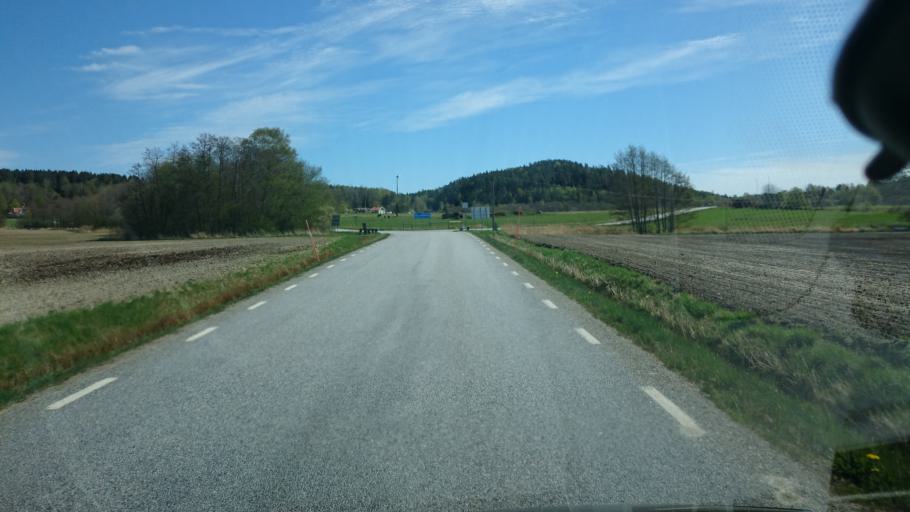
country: SE
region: Vaestra Goetaland
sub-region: Munkedals Kommun
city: Munkedal
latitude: 58.3785
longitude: 11.6759
